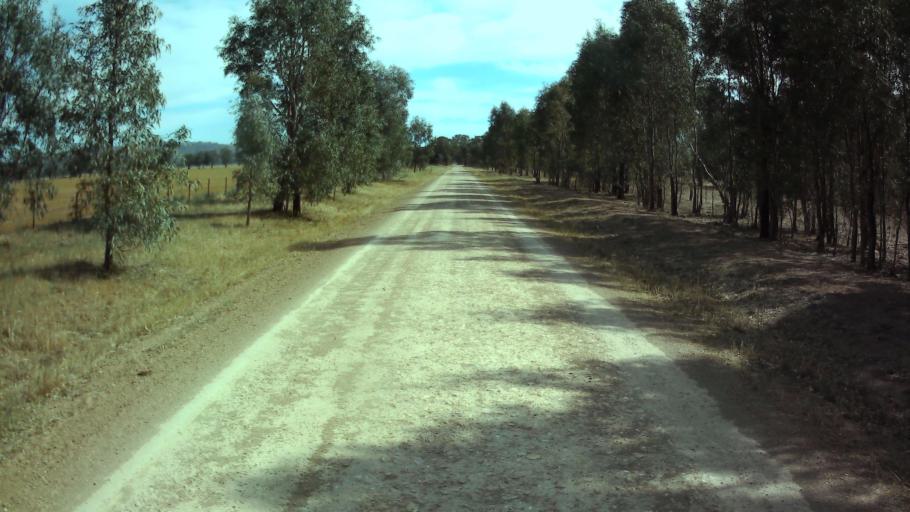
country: AU
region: New South Wales
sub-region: Weddin
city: Grenfell
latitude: -33.7070
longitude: 148.3011
